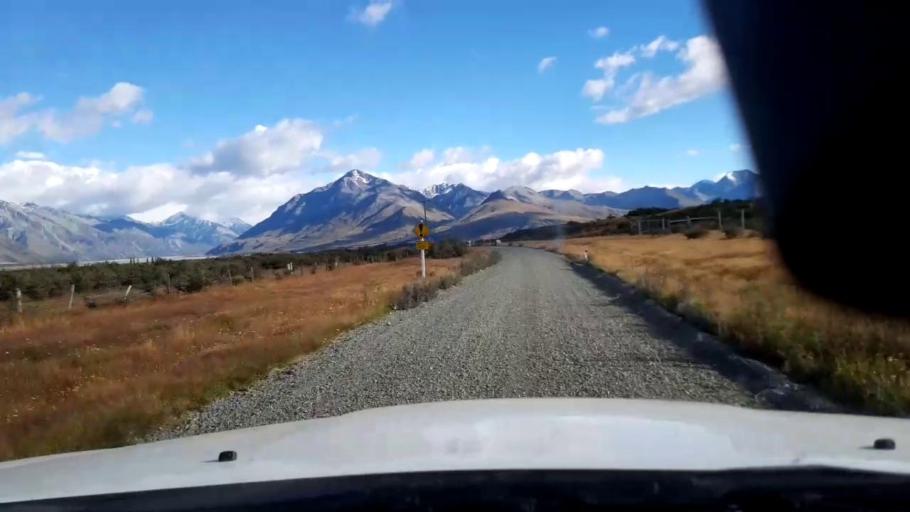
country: NZ
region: Canterbury
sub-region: Timaru District
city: Pleasant Point
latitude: -43.7643
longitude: 170.5699
